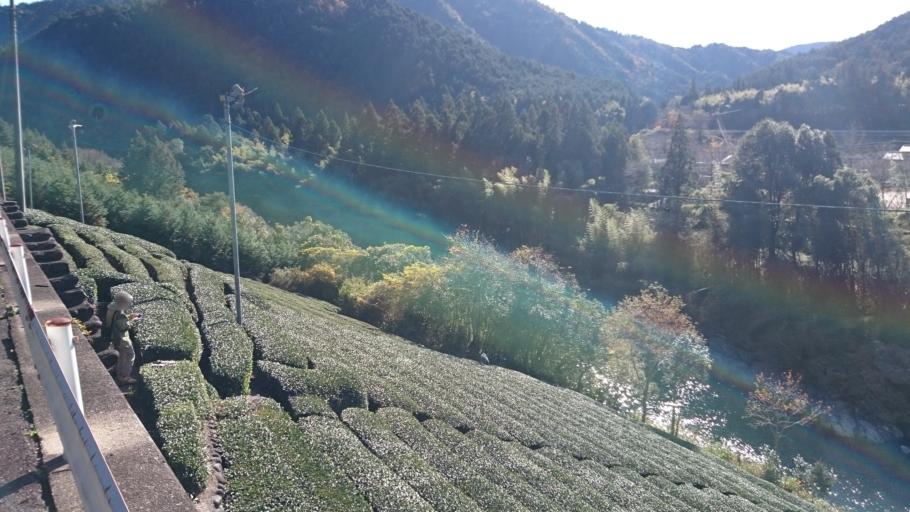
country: JP
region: Gifu
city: Mitake
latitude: 35.6138
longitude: 137.1743
